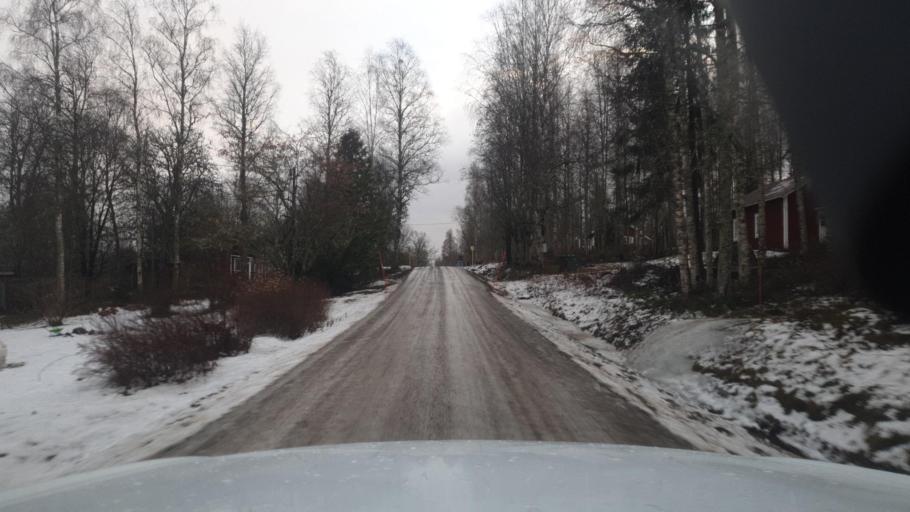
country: SE
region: Vaermland
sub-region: Torsby Kommun
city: Torsby
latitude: 59.9670
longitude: 12.8755
